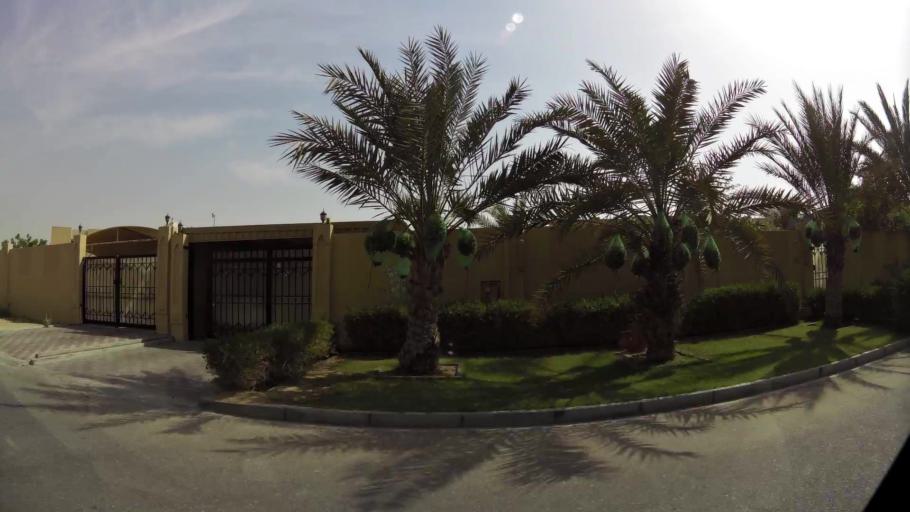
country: AE
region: Ash Shariqah
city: Sharjah
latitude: 25.2616
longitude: 55.4337
